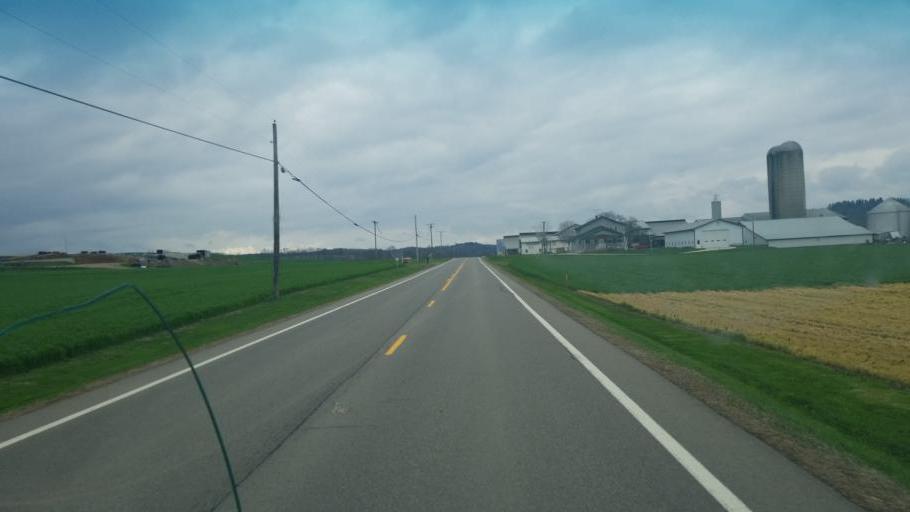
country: US
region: Ohio
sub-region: Ashland County
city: Loudonville
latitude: 40.6529
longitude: -82.2812
